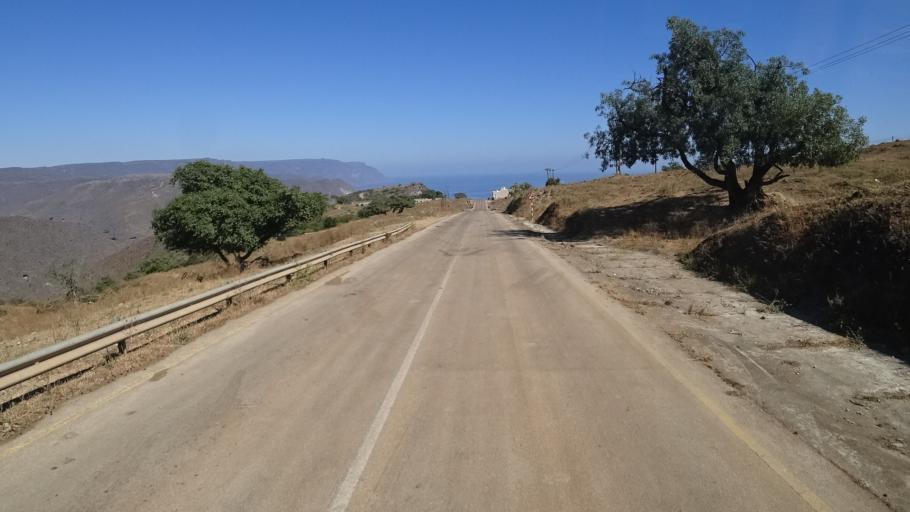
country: YE
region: Al Mahrah
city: Hawf
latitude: 16.7440
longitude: 53.3748
